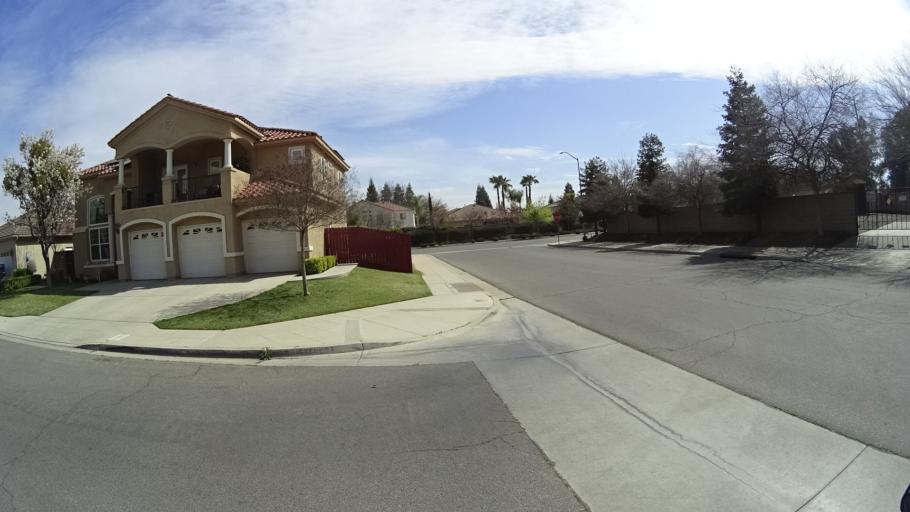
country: US
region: California
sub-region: Fresno County
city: Biola
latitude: 36.8469
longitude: -119.9002
